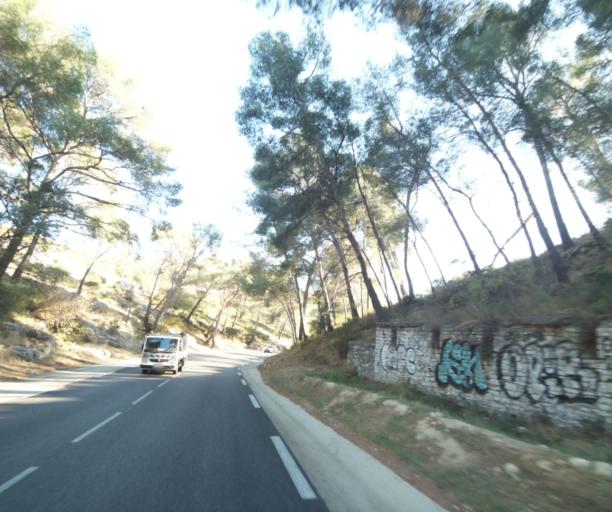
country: FR
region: Provence-Alpes-Cote d'Azur
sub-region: Departement des Bouches-du-Rhone
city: Cassis
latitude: 43.2143
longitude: 5.5790
